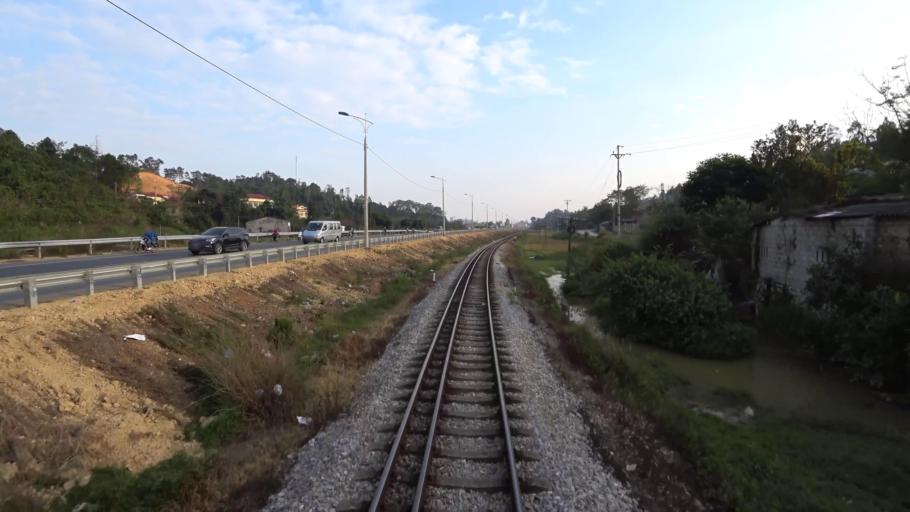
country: VN
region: Lang Son
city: Thi Tran Cao Loc
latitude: 21.8997
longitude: 106.7403
